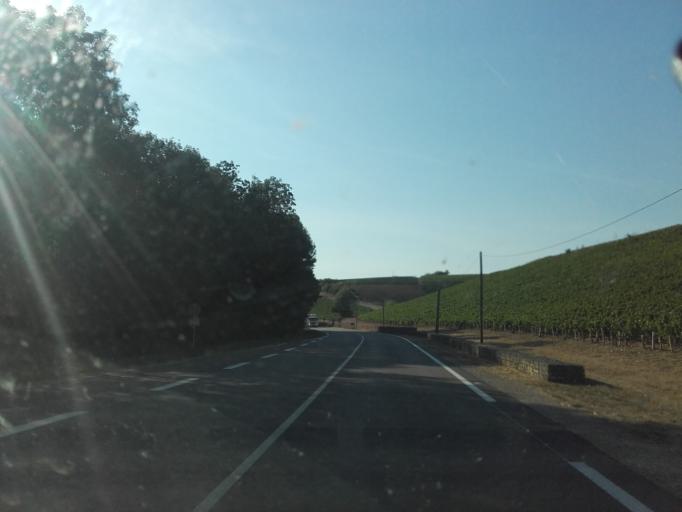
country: FR
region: Bourgogne
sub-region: Departement de l'Yonne
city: Chablis
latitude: 47.8216
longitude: 3.8016
